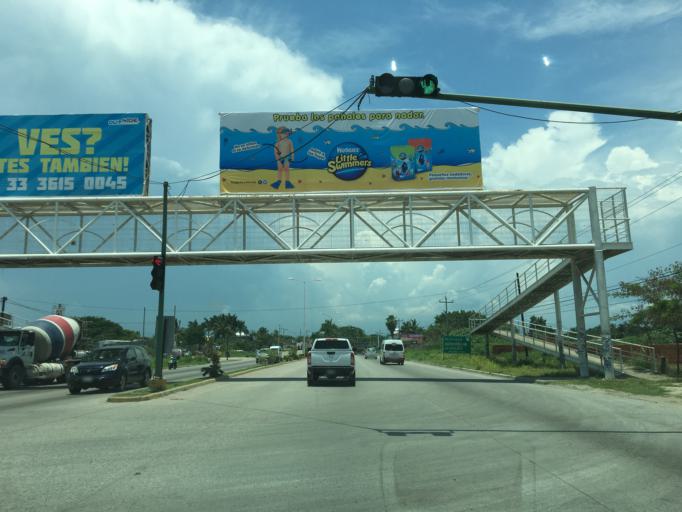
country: MX
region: Nayarit
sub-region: Bahia de Banderas
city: San Clemente de Lima
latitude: 20.7414
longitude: -105.2950
